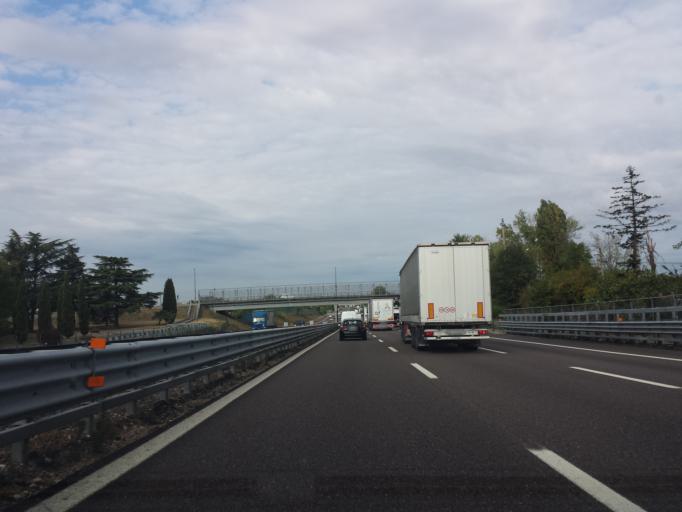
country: IT
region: Lombardy
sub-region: Provincia di Brescia
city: Calcinato
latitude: 45.4647
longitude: 10.4129
